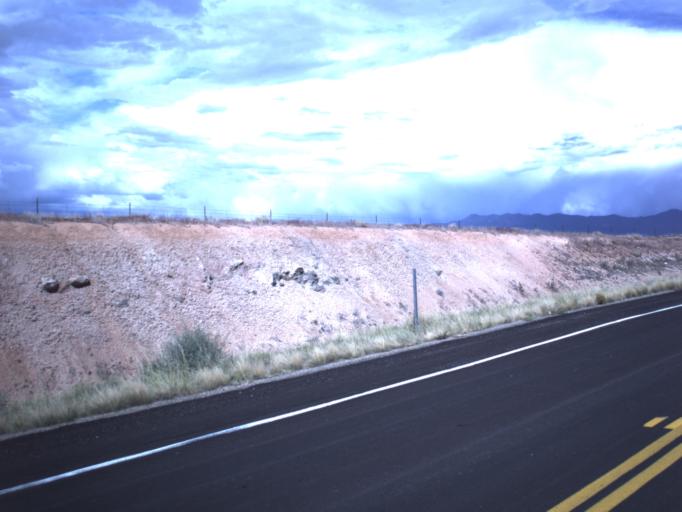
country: US
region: Colorado
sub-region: Montezuma County
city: Towaoc
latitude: 37.1719
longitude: -109.0937
